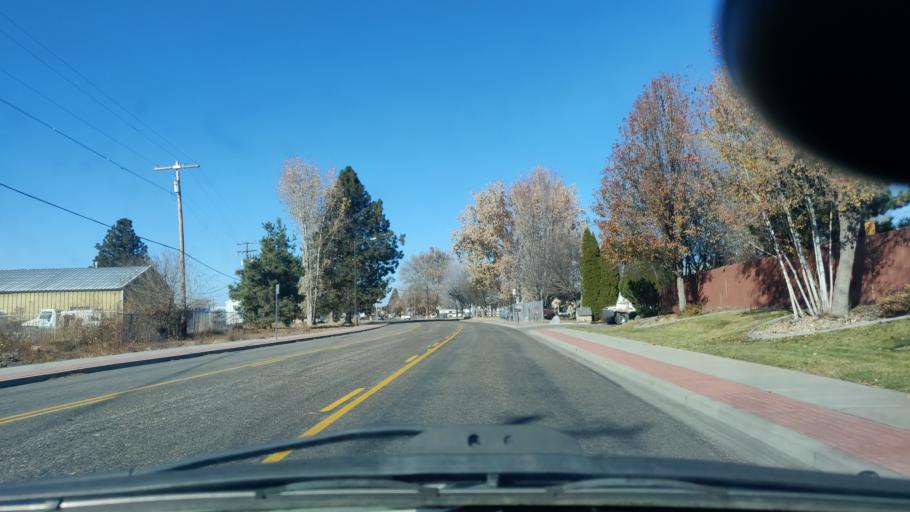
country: US
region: Idaho
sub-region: Ada County
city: Garden City
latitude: 43.6438
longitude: -116.2602
